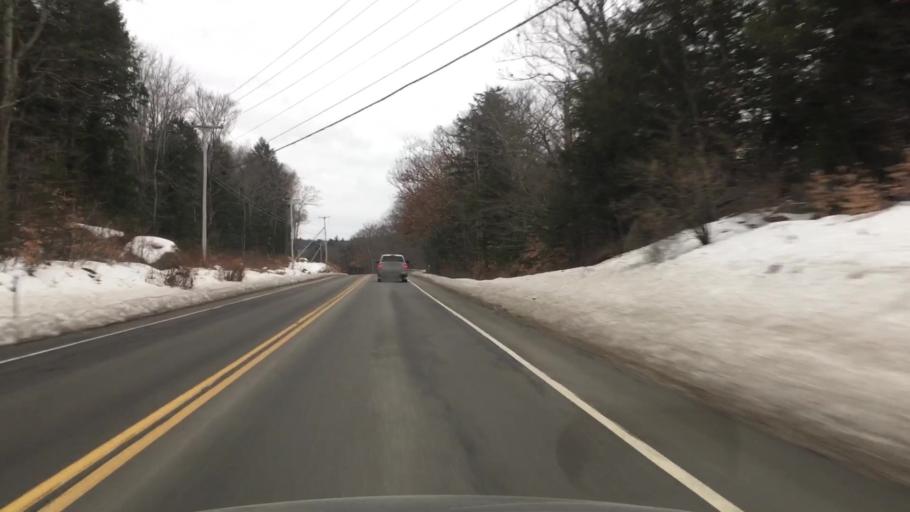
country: US
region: New Hampshire
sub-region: Merrimack County
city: Newbury
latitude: 43.3059
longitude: -72.0128
